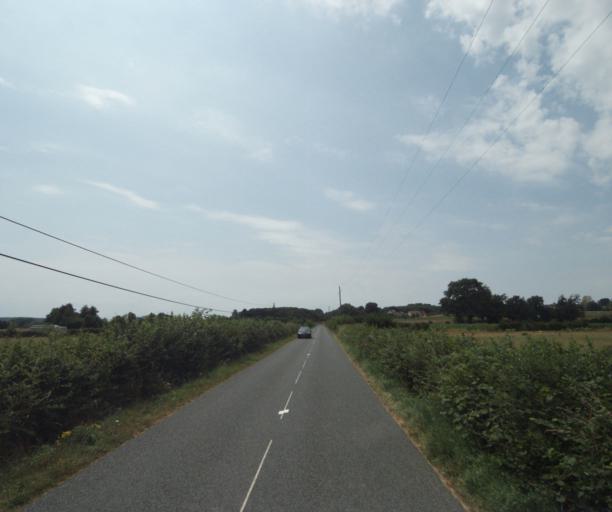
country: FR
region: Bourgogne
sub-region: Departement de Saone-et-Loire
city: Gueugnon
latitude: 46.5865
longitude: 4.0508
